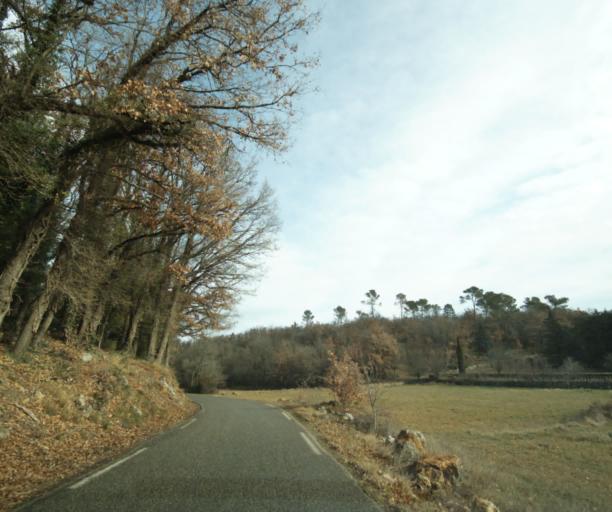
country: FR
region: Provence-Alpes-Cote d'Azur
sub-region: Departement du Var
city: Rougiers
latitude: 43.4152
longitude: 5.8695
